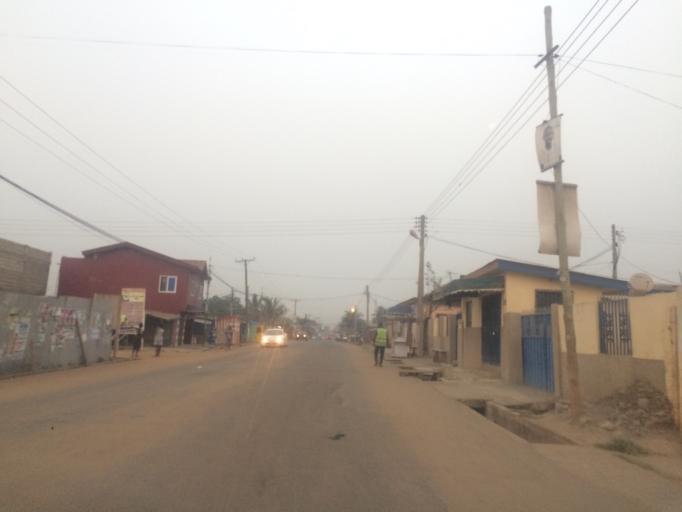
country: GH
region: Greater Accra
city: Teshi Old Town
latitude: 5.5912
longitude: -0.1039
